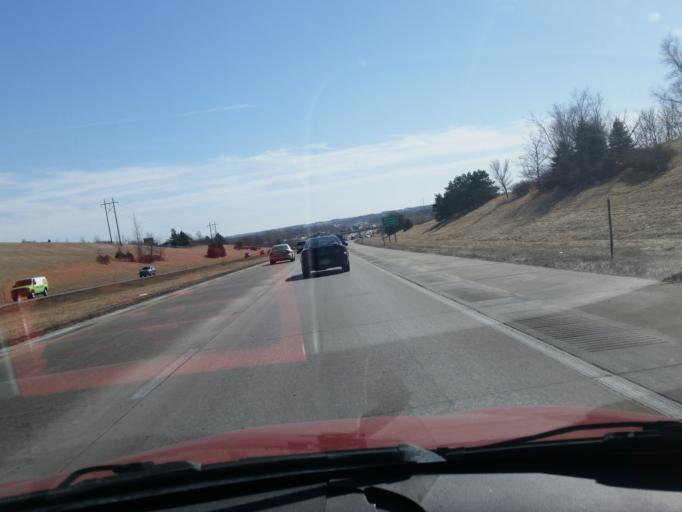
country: US
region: Nebraska
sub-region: Sarpy County
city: Offutt Air Force Base
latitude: 41.1686
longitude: -95.9393
